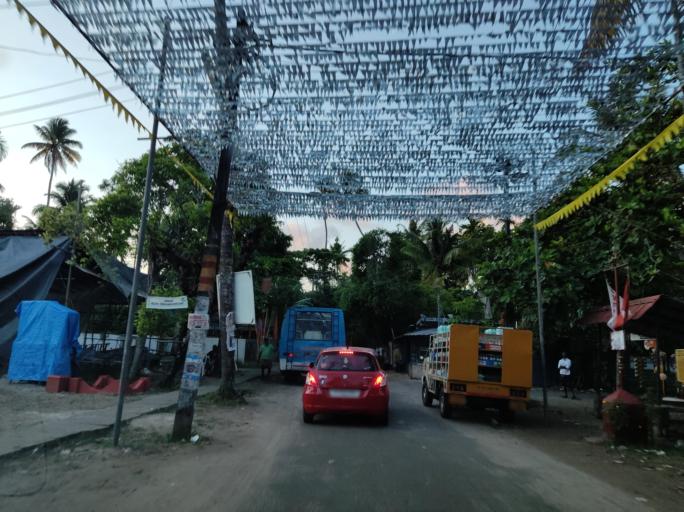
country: IN
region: Kerala
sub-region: Alappuzha
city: Vayalar
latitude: 9.7369
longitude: 76.2892
